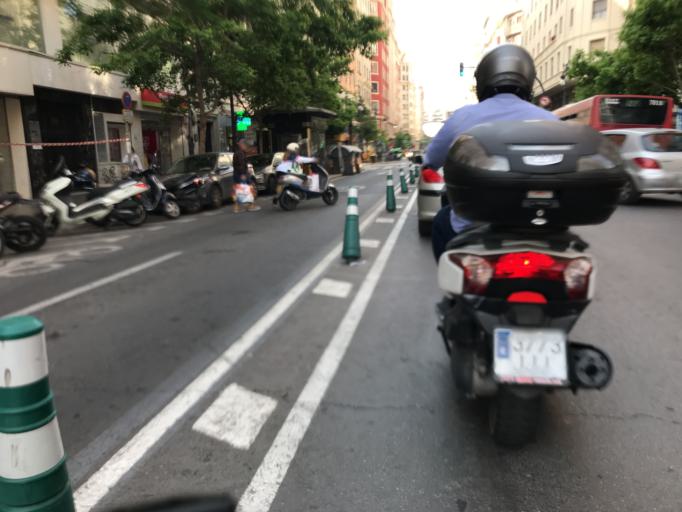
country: ES
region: Valencia
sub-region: Provincia de Valencia
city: Valencia
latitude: 39.4729
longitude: -0.3798
